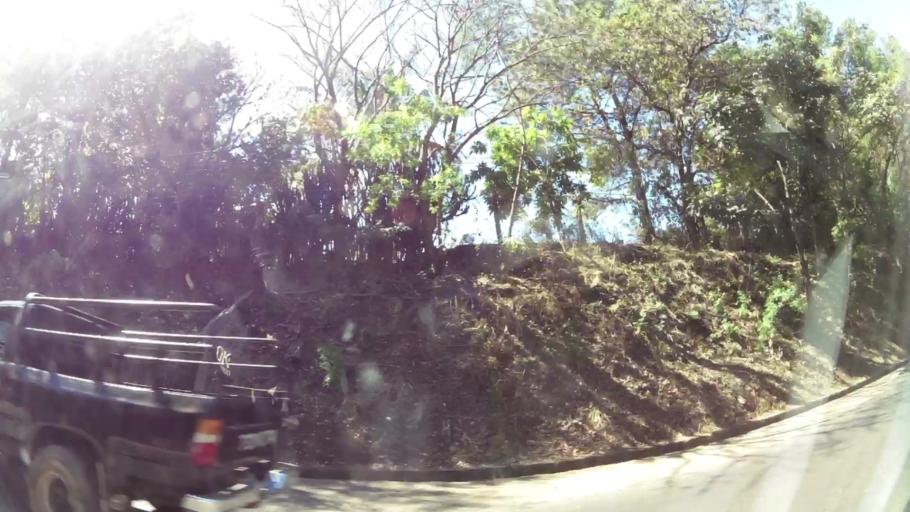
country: SV
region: Ahuachapan
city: Ahuachapan
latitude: 13.9231
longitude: -89.8423
